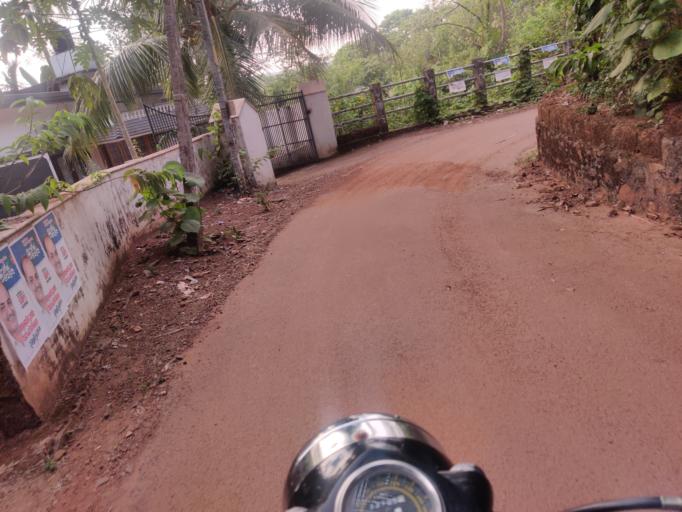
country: IN
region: Kerala
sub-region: Kozhikode
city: Mavoor
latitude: 11.2594
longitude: 75.9500
